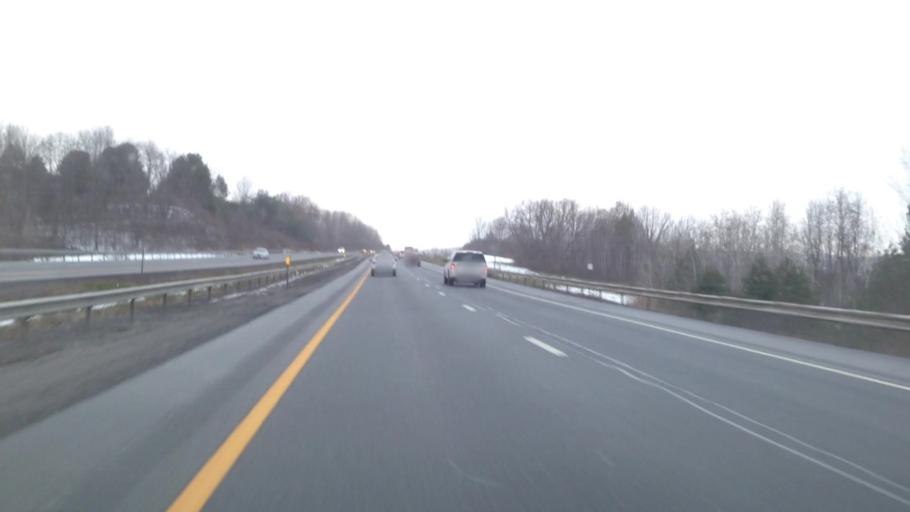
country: US
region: New York
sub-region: Montgomery County
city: Fort Plain
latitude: 42.9480
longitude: -74.6313
